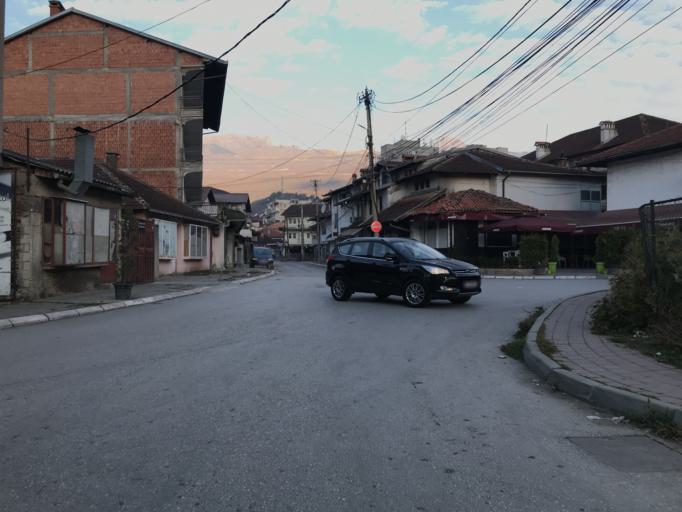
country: XK
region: Pec
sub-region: Komuna e Pejes
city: Peje
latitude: 42.6609
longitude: 20.2995
